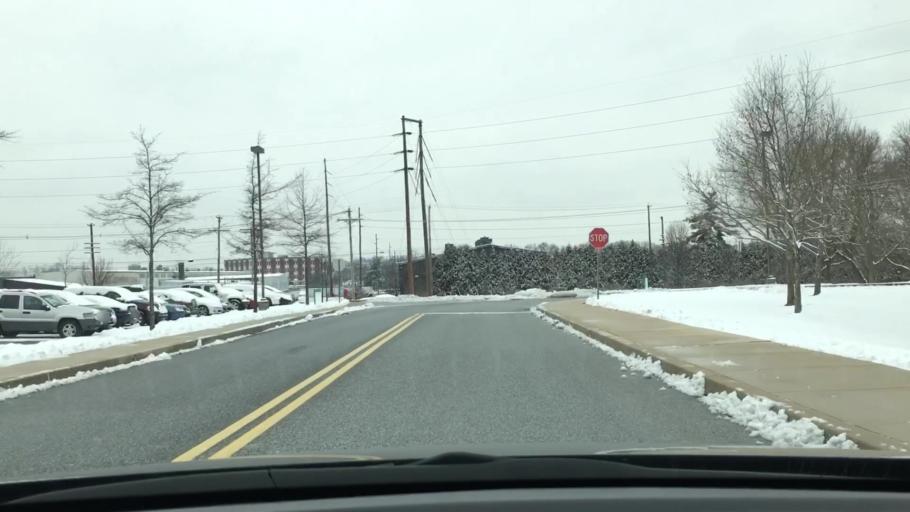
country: US
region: Pennsylvania
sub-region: York County
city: Grantley
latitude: 39.9454
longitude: -76.7392
